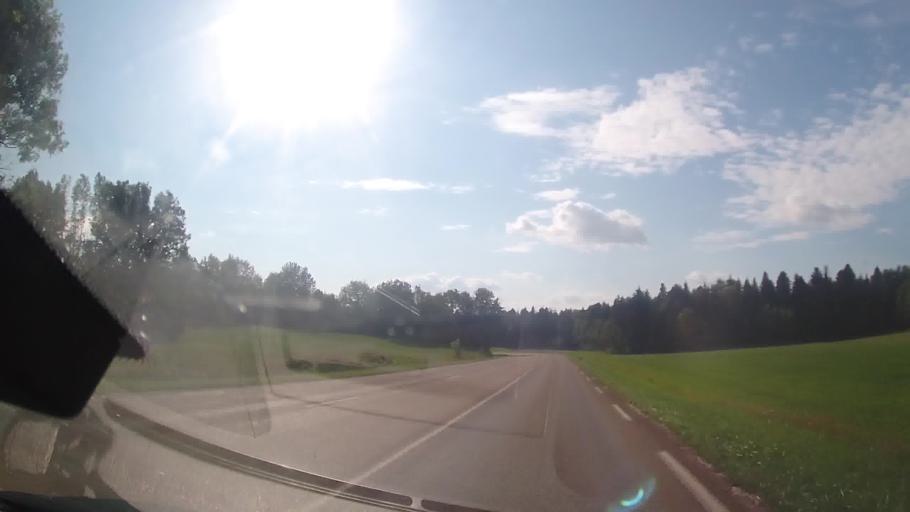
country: FR
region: Franche-Comte
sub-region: Departement du Jura
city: Clairvaux-les-Lacs
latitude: 46.5821
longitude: 5.7917
